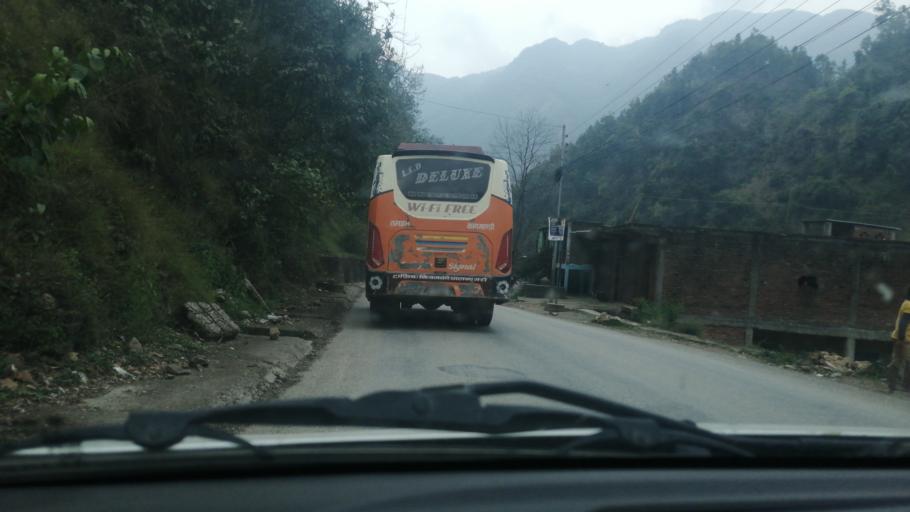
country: NP
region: Western Region
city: Tansen
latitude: 27.8068
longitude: 83.5149
